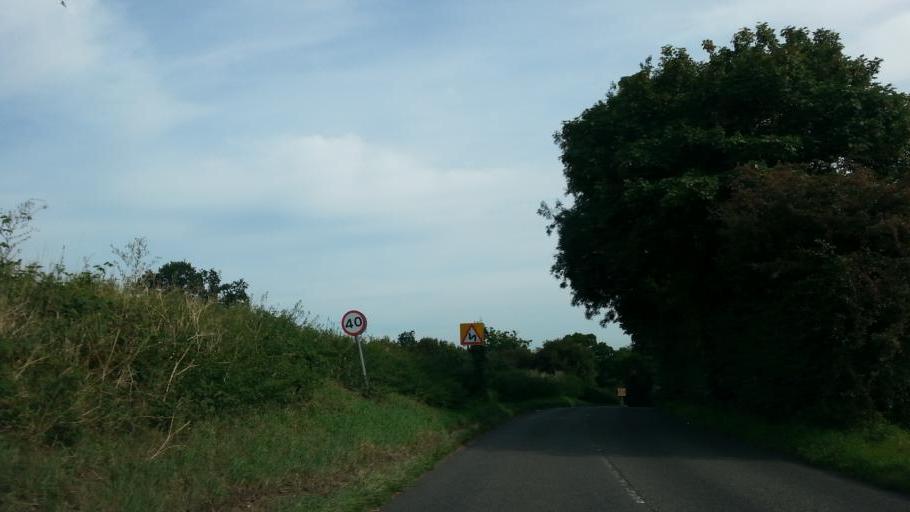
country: GB
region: England
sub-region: Suffolk
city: Bramford
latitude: 52.0536
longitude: 1.0967
